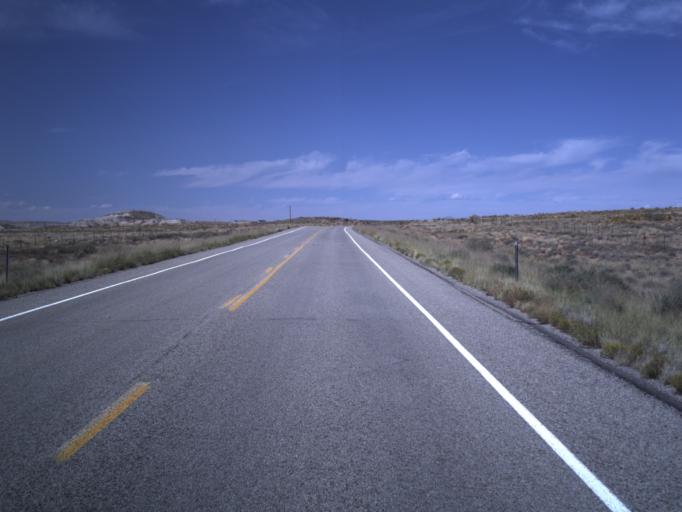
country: US
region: Colorado
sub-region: Montezuma County
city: Towaoc
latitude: 37.1592
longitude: -109.0630
